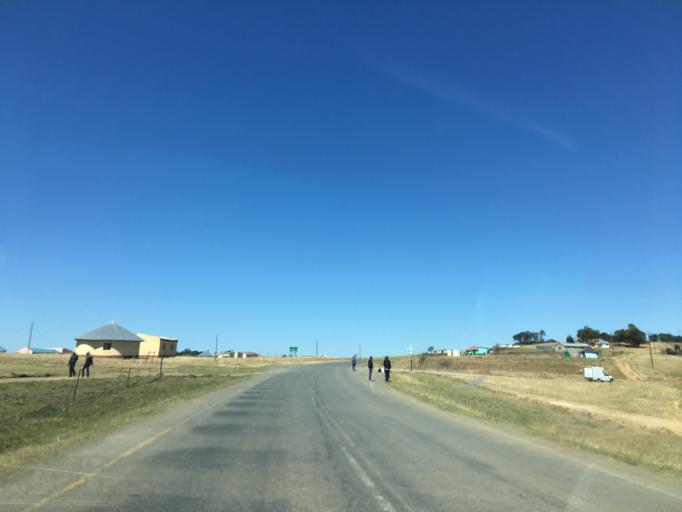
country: ZA
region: Eastern Cape
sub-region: Chris Hani District Municipality
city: Cala
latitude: -31.5565
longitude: 27.8964
